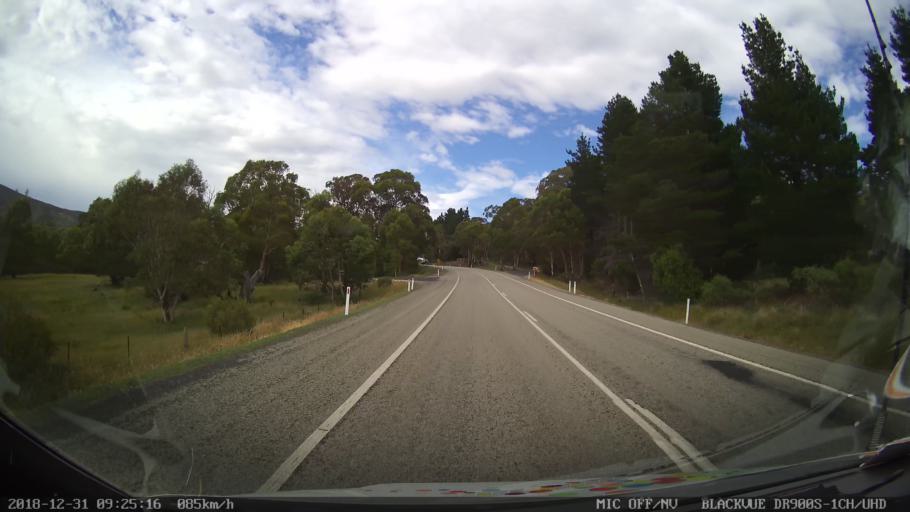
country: AU
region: New South Wales
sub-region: Snowy River
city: Jindabyne
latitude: -36.4420
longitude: 148.5094
